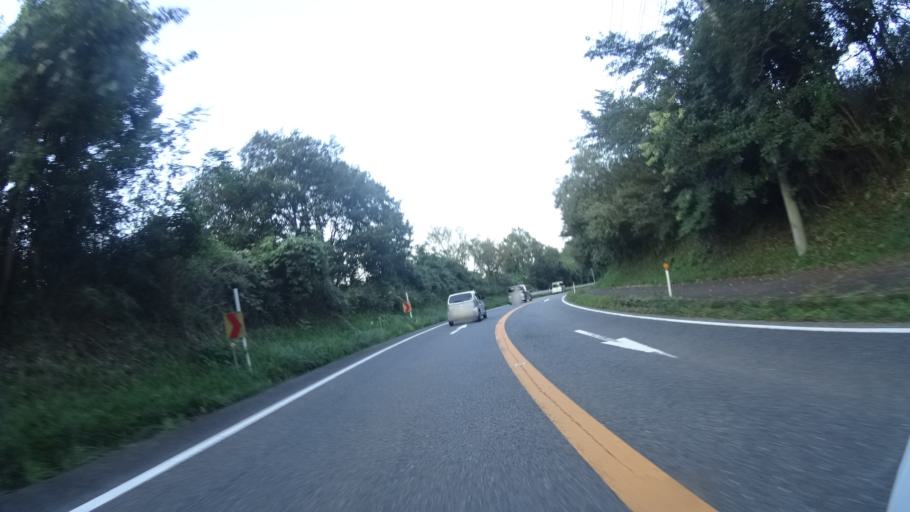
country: JP
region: Oita
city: Hiji
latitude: 33.3513
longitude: 131.4429
